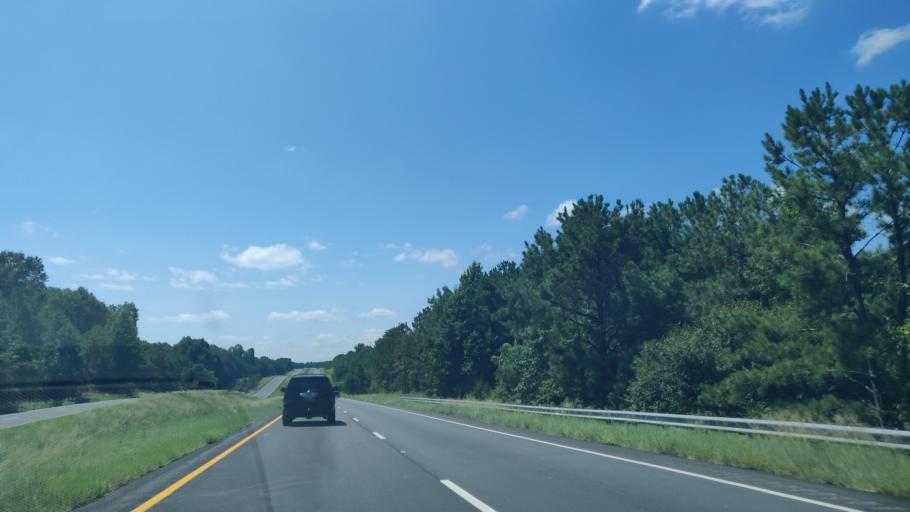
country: US
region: Georgia
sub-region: Chattahoochee County
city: Cusseta
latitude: 32.2111
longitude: -84.7069
